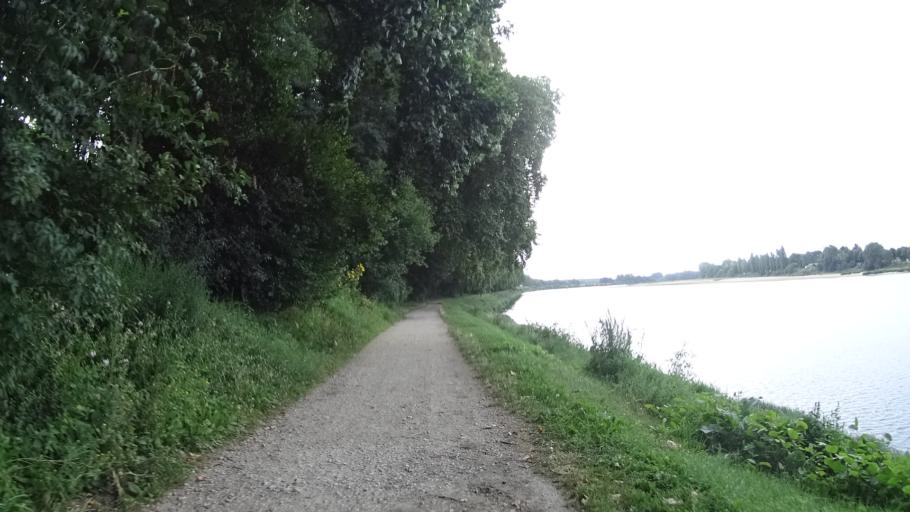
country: FR
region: Centre
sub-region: Departement du Loiret
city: Chateauneuf-sur-Loire
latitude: 47.8599
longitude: 2.2272
